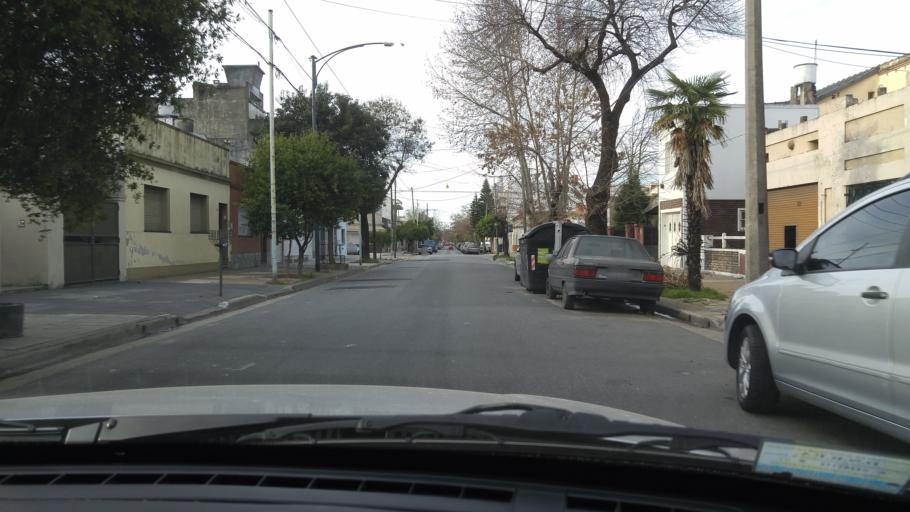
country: AR
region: Buenos Aires F.D.
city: Villa Santa Rita
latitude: -34.6273
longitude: -58.5170
